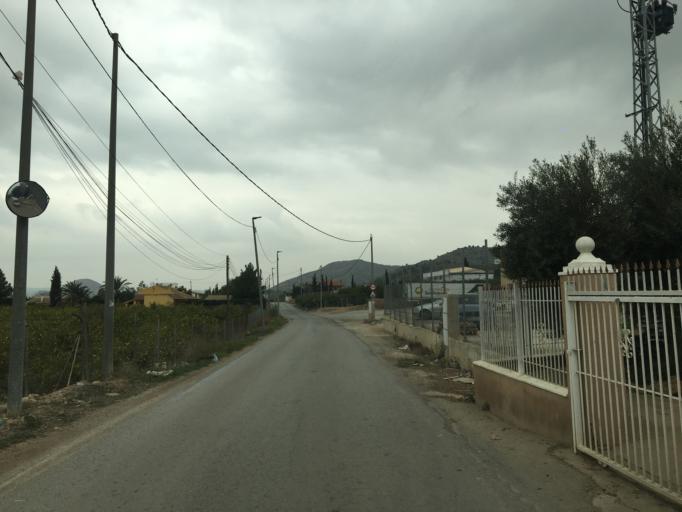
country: ES
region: Murcia
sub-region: Murcia
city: Santomera
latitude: 38.0758
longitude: -1.0442
